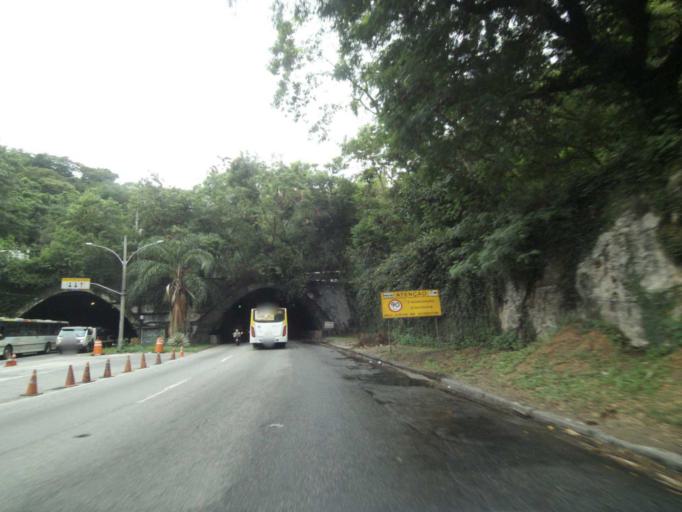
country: BR
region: Rio de Janeiro
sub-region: Rio De Janeiro
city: Rio de Janeiro
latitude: -22.9351
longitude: -43.2098
